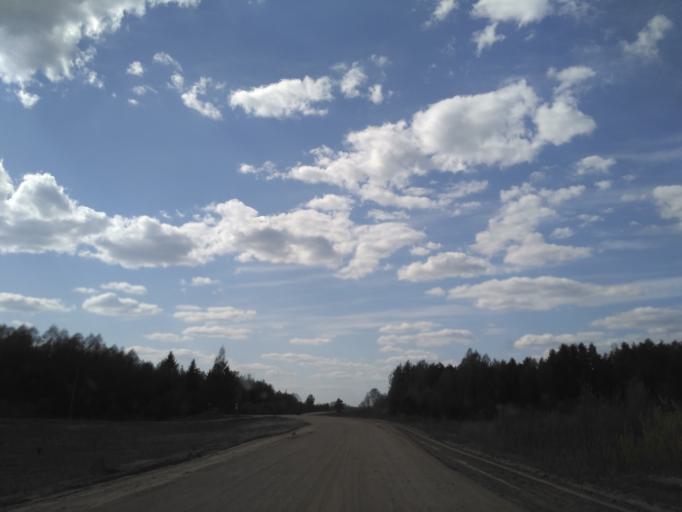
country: BY
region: Minsk
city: Narach
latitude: 54.9928
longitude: 26.5711
